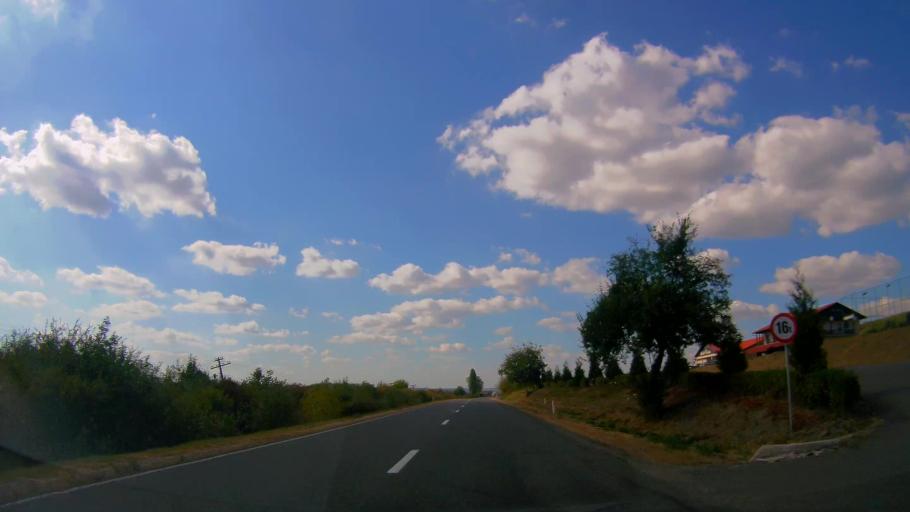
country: RO
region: Salaj
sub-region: Comuna Sarmasag
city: Sarmasag
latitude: 47.3303
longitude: 22.8607
